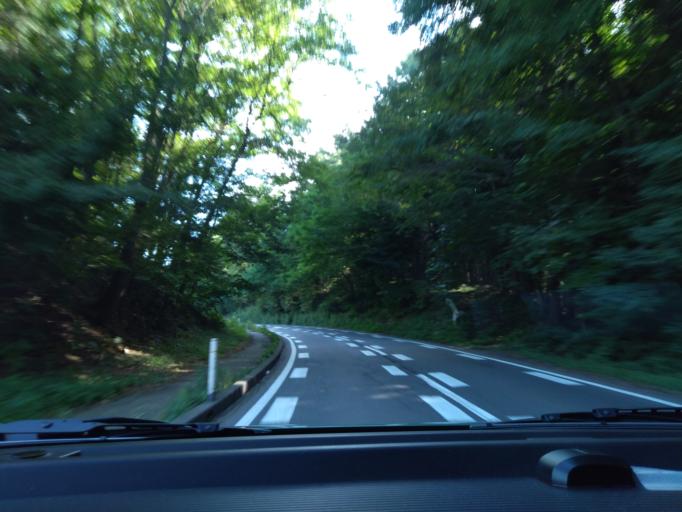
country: JP
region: Iwate
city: Morioka-shi
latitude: 39.6152
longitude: 141.0910
